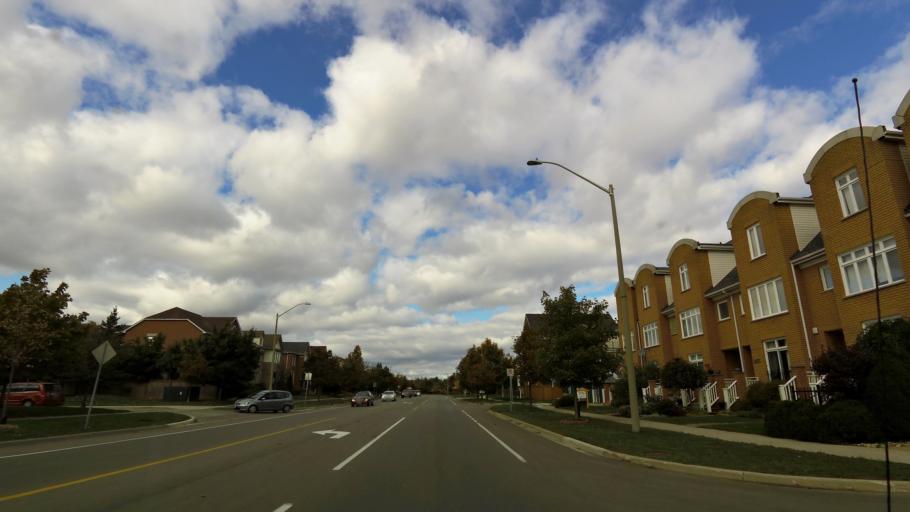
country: CA
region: Ontario
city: Oakville
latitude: 43.4733
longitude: -79.7238
